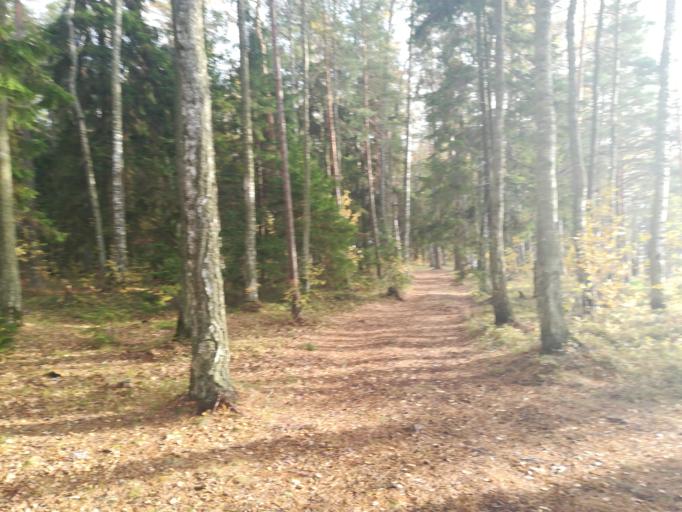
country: RU
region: Leningrad
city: Ust'-Luga
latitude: 59.7529
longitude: 28.1494
